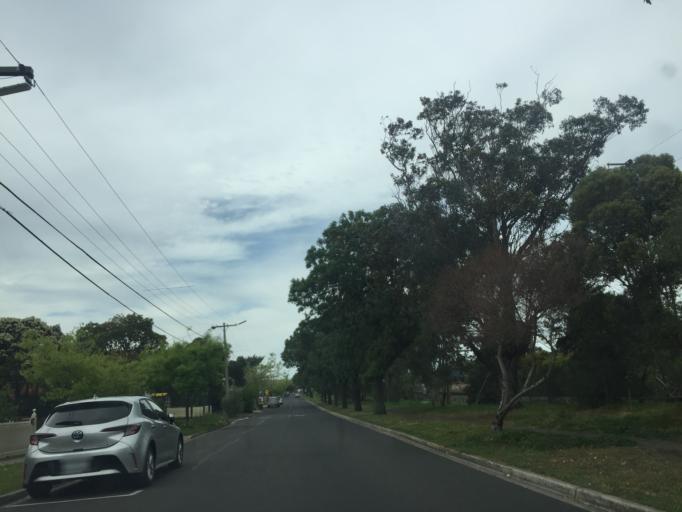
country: AU
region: Victoria
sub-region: Darebin
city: Northcote
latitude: -37.7790
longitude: 145.0027
